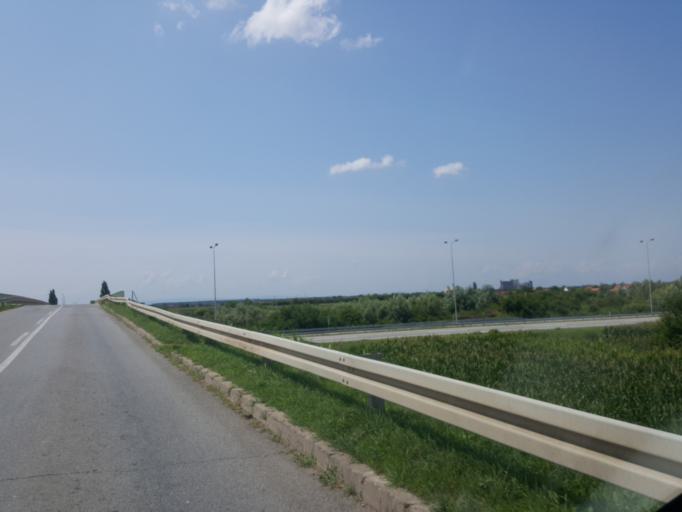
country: RS
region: Autonomna Pokrajina Vojvodina
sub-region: Sremski Okrug
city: Sremska Mitrovica
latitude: 45.0004
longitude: 19.6424
